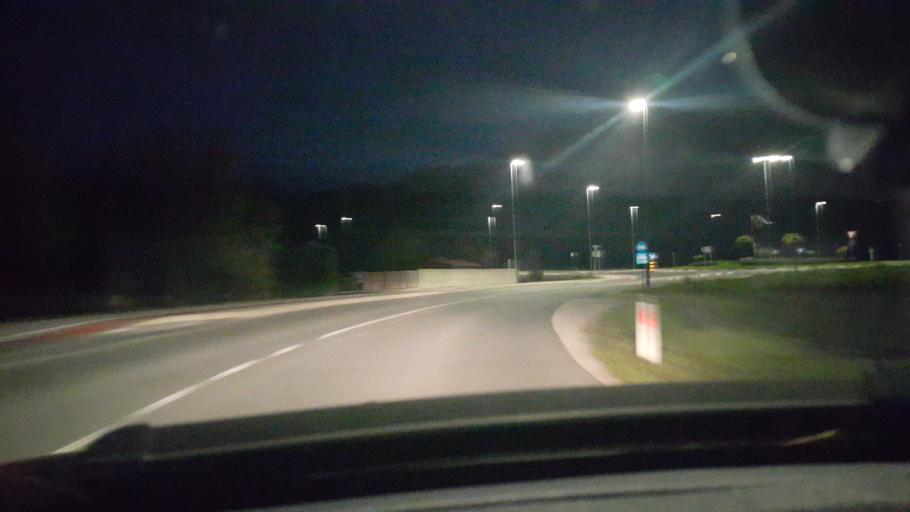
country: SI
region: Zrece
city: Zrece
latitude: 46.3603
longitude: 15.3703
